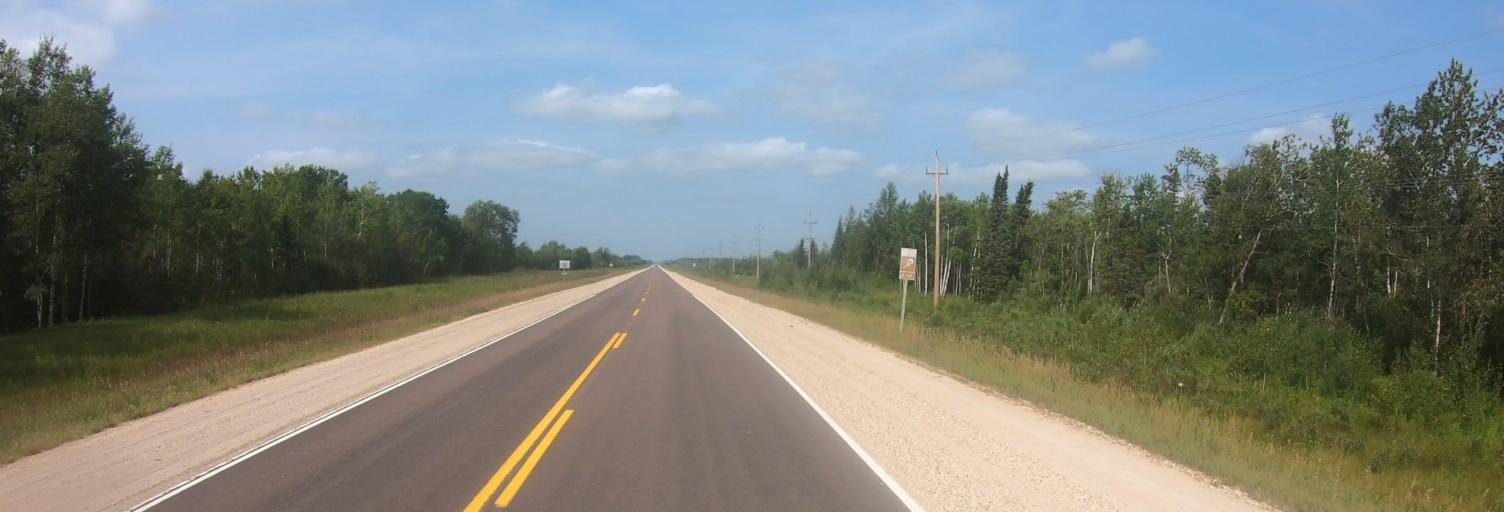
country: CA
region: Manitoba
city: La Broquerie
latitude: 49.2670
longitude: -96.3715
